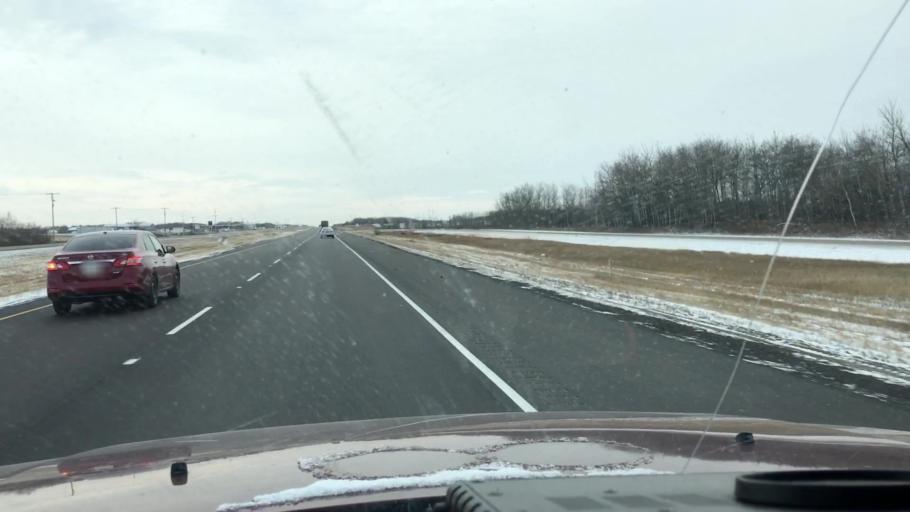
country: CA
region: Saskatchewan
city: Saskatoon
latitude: 51.9722
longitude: -106.5551
